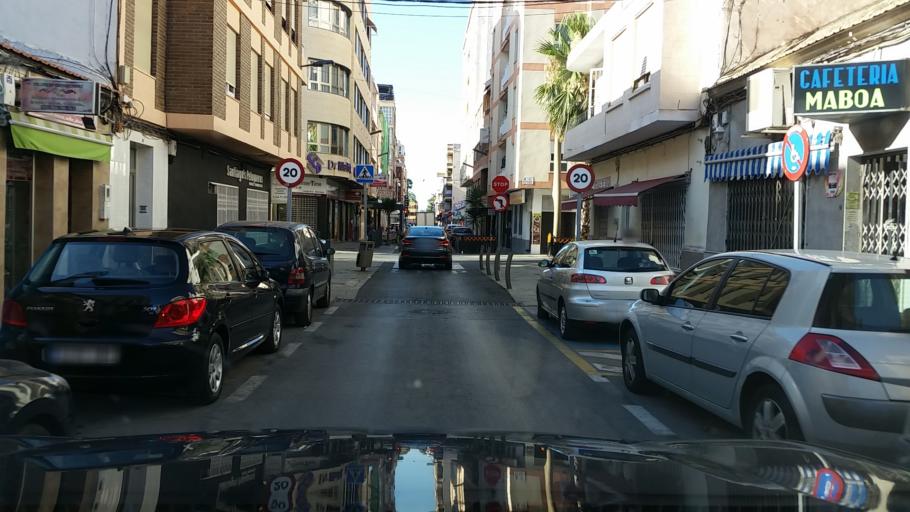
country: ES
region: Valencia
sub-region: Provincia de Alicante
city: Torrevieja
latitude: 37.9782
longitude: -0.6806
